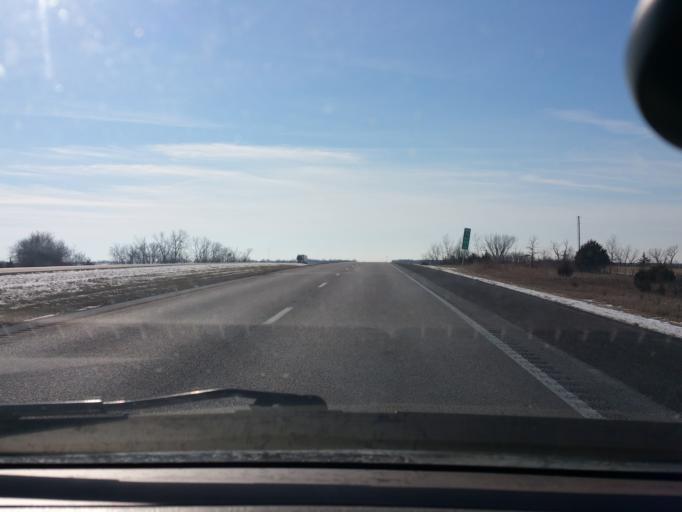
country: US
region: Missouri
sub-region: Daviess County
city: Gallatin
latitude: 39.9221
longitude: -94.1396
